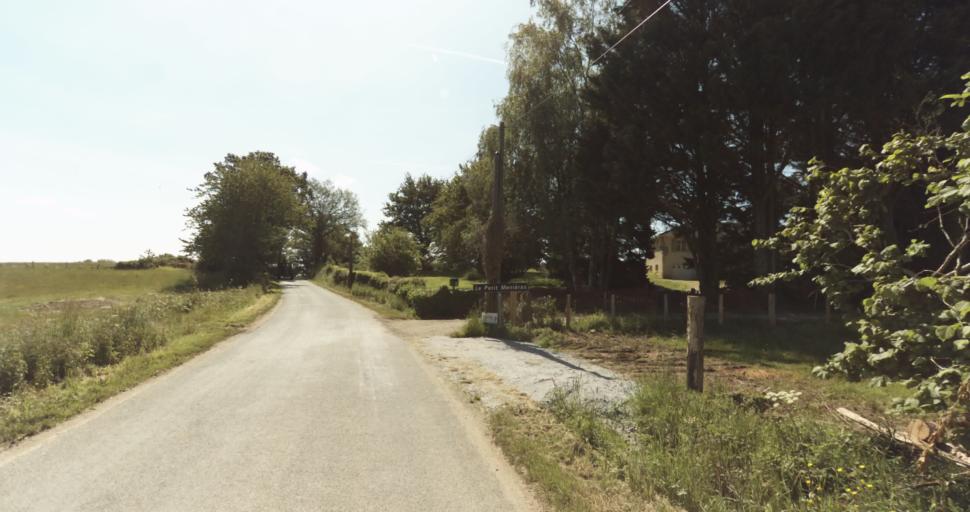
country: FR
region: Limousin
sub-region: Departement de la Haute-Vienne
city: Le Vigen
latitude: 45.7131
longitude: 1.2912
